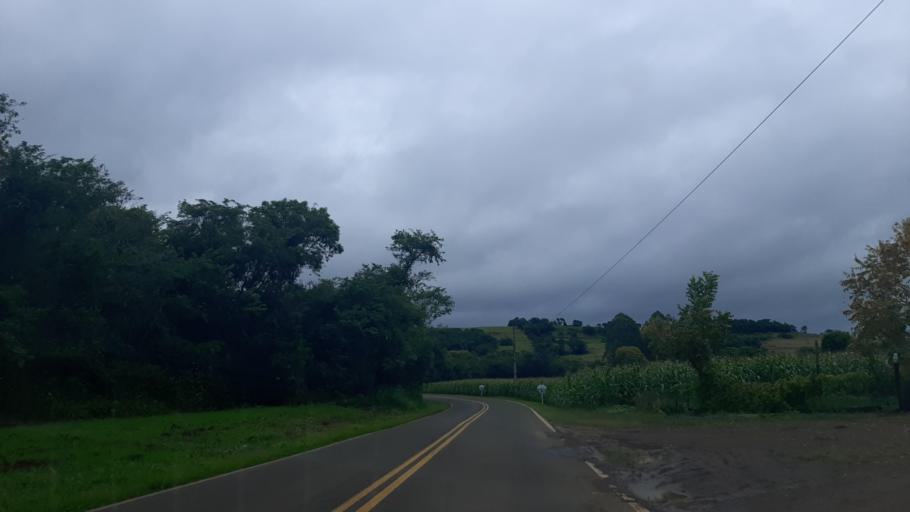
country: BR
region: Parana
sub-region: Ampere
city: Ampere
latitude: -25.9986
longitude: -53.4392
